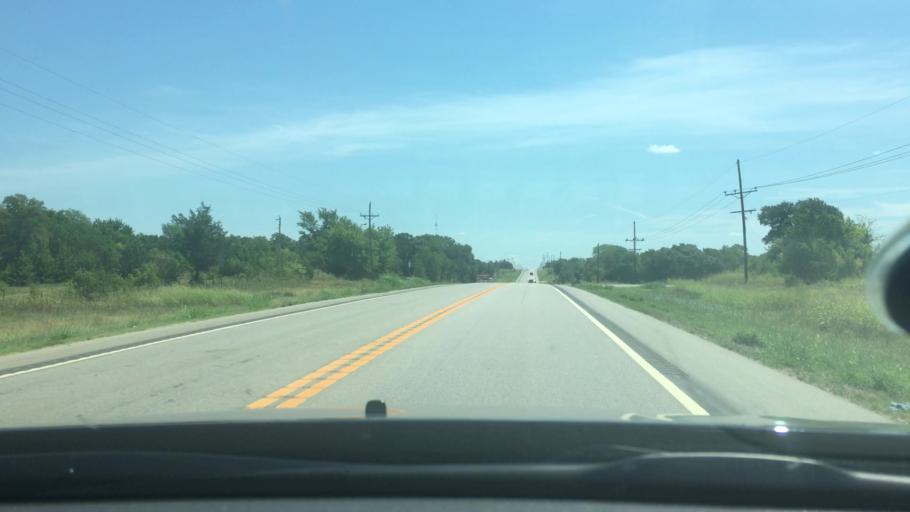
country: US
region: Oklahoma
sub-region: Bryan County
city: Durant
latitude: 33.9975
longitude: -96.2872
